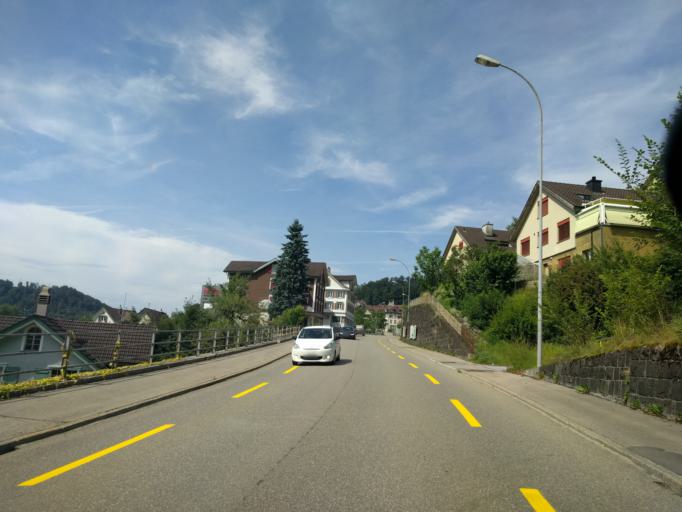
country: CH
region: Saint Gallen
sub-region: Wahlkreis Toggenburg
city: Lichtensteig
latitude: 47.3194
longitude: 9.0873
